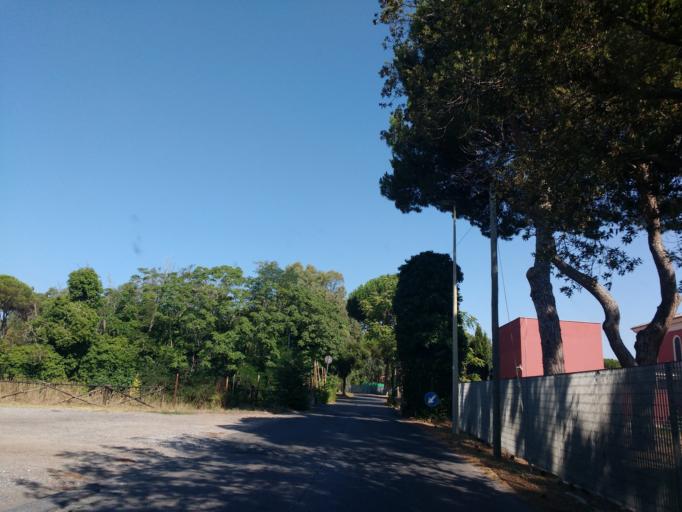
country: IT
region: Latium
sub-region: Citta metropolitana di Roma Capitale
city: Acilia-Castel Fusano-Ostia Antica
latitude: 41.7459
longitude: 12.3183
